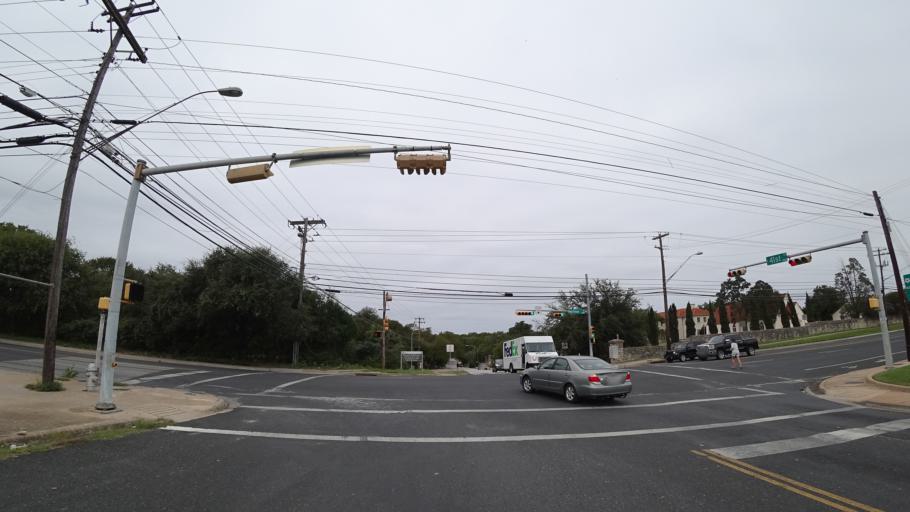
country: US
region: Texas
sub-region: Travis County
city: Austin
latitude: 30.2996
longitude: -97.7223
